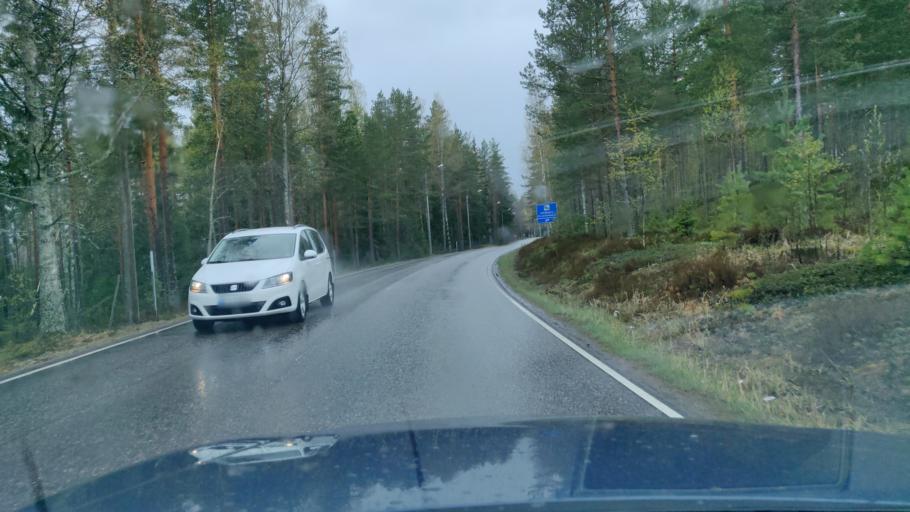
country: FI
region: Uusimaa
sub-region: Helsinki
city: Nurmijaervi
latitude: 60.5046
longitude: 24.7000
